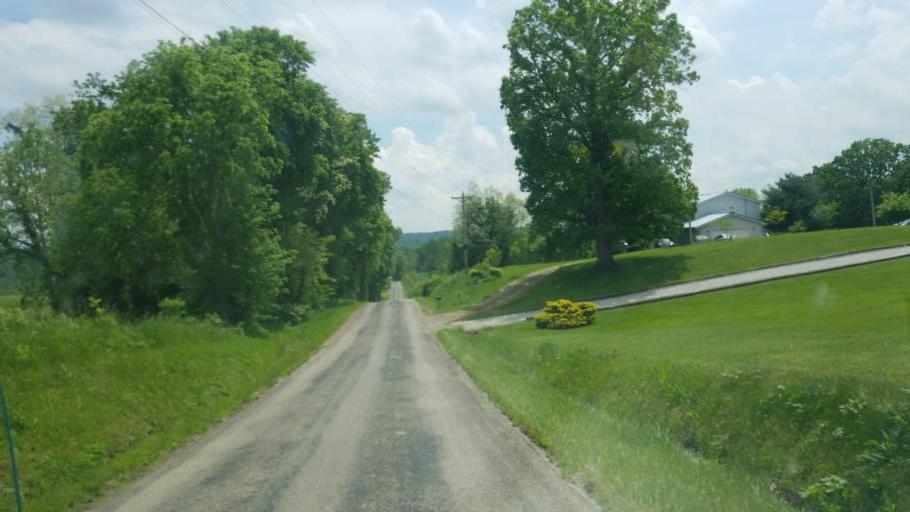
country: US
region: Ohio
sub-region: Ashland County
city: Ashland
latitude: 40.7775
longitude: -82.3396
